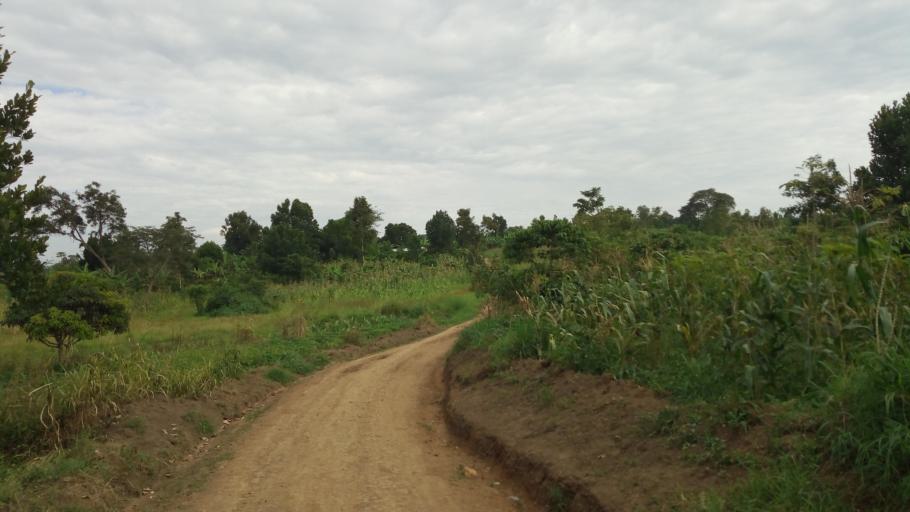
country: UG
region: Central Region
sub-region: Kiboga District
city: Kiboga
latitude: 0.7594
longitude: 31.6985
